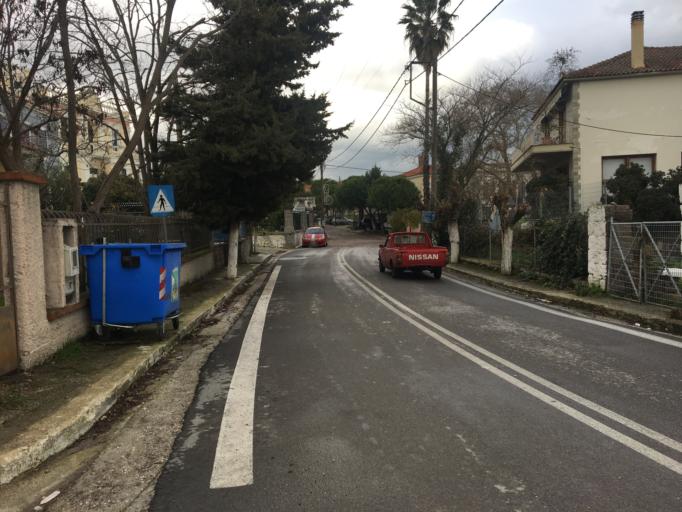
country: GR
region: North Aegean
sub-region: Nomos Lesvou
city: Agia Paraskevi
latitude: 39.2460
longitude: 26.2691
